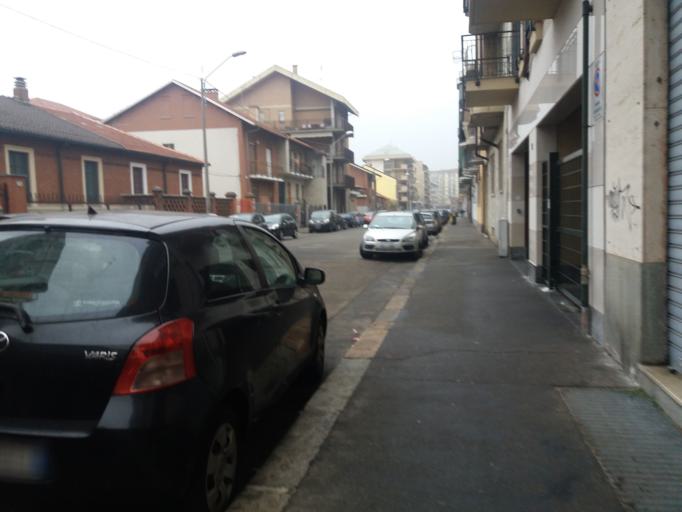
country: IT
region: Piedmont
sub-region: Provincia di Torino
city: Lesna
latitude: 45.0609
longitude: 7.6207
